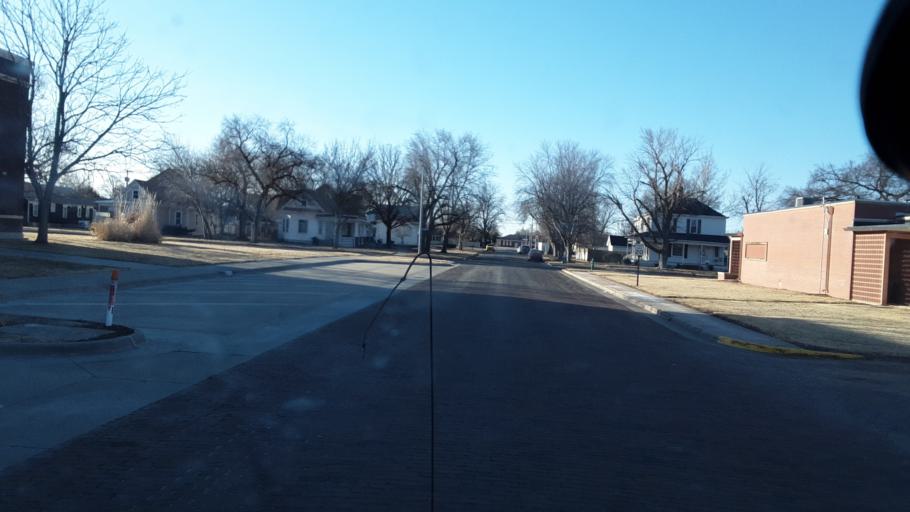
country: US
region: Kansas
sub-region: Barton County
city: Ellinwood
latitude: 38.3563
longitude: -98.5793
